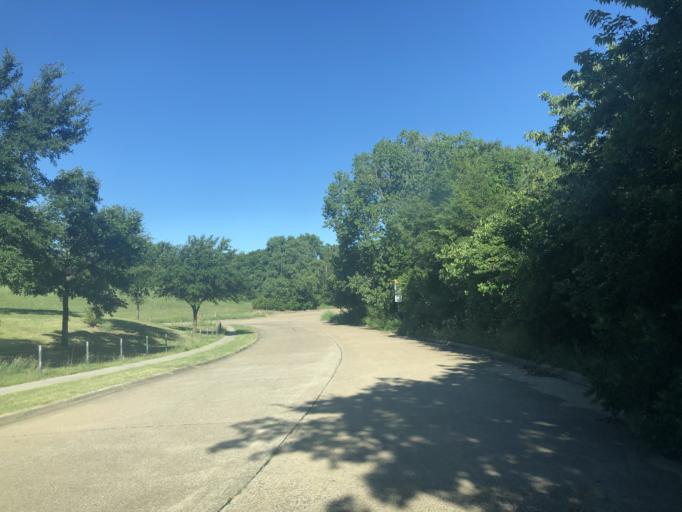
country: US
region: Texas
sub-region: Dallas County
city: Duncanville
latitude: 32.6669
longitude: -96.9295
